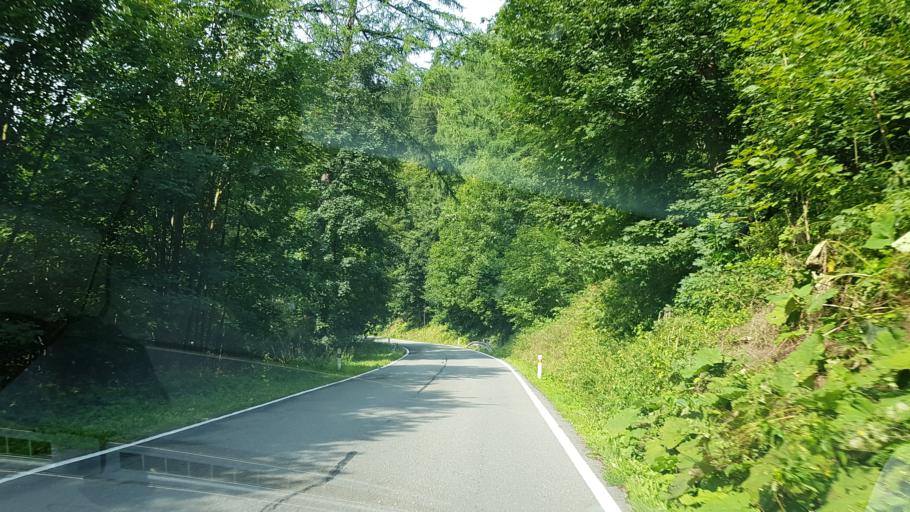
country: CZ
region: Olomoucky
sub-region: Okres Jesenik
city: Jesenik
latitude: 50.2088
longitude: 17.2476
